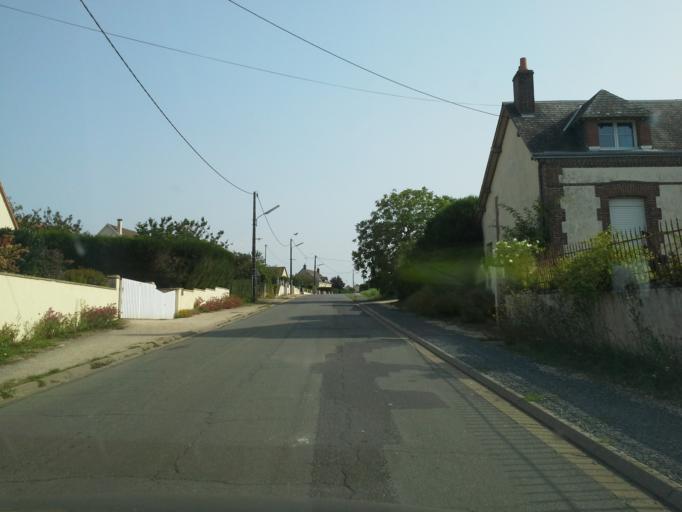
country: FR
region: Centre
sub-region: Departement du Loir-et-Cher
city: Aze
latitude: 47.8943
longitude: 1.0273
